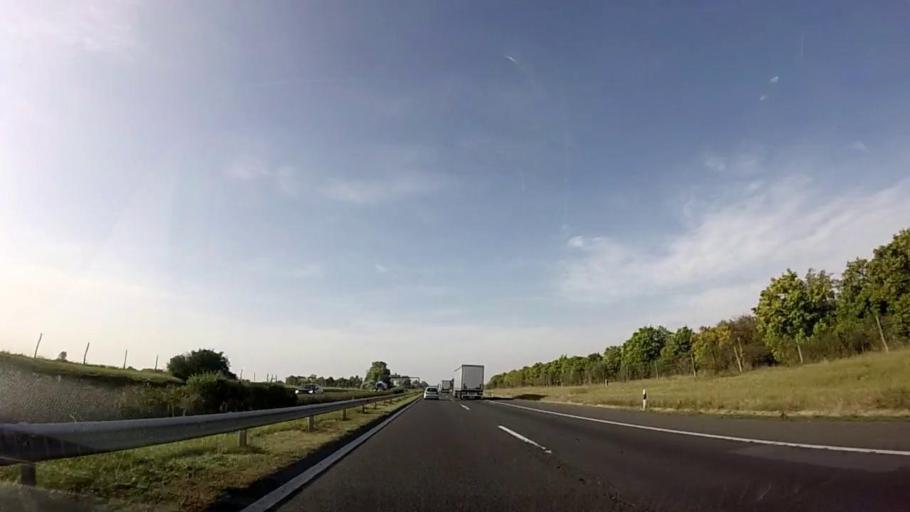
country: HU
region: Fejer
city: Pakozd
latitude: 47.1905
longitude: 18.5045
